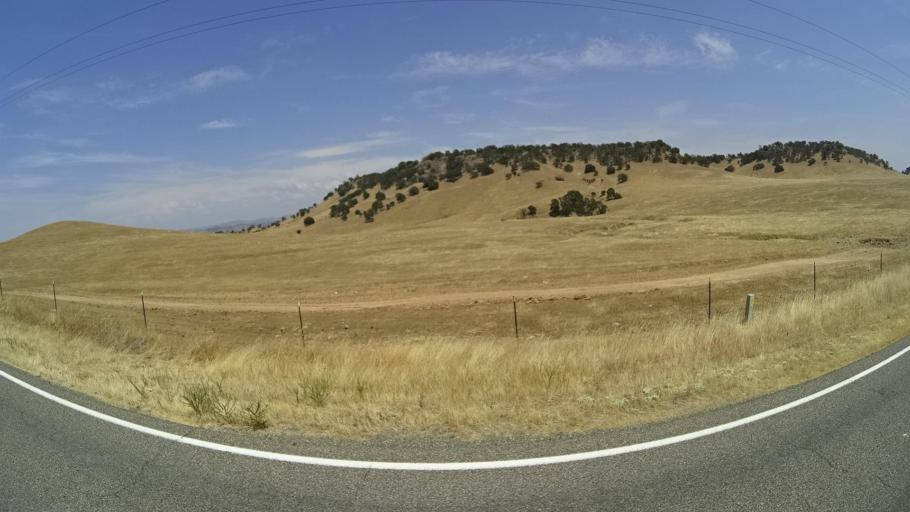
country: US
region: California
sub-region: Merced County
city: Planada
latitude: 37.4994
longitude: -120.3127
